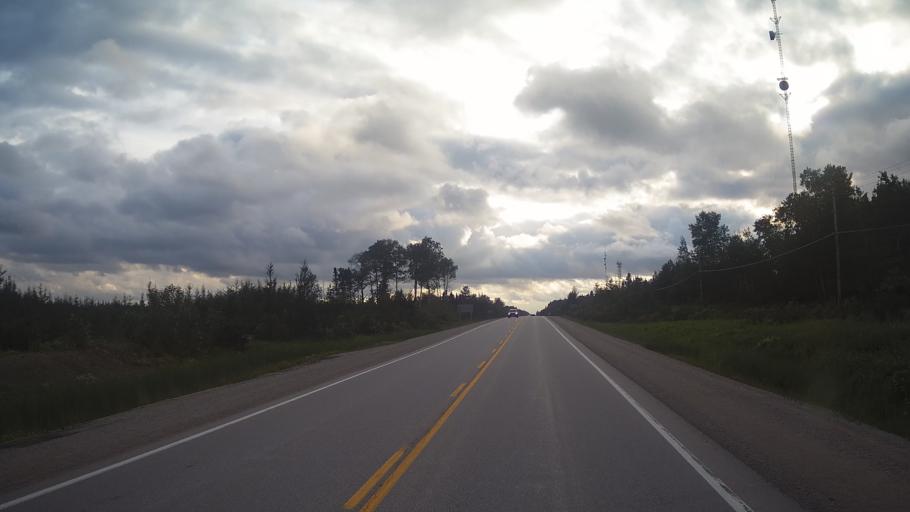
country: CA
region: Ontario
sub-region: Rainy River District
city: Atikokan
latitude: 49.0509
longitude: -90.4874
